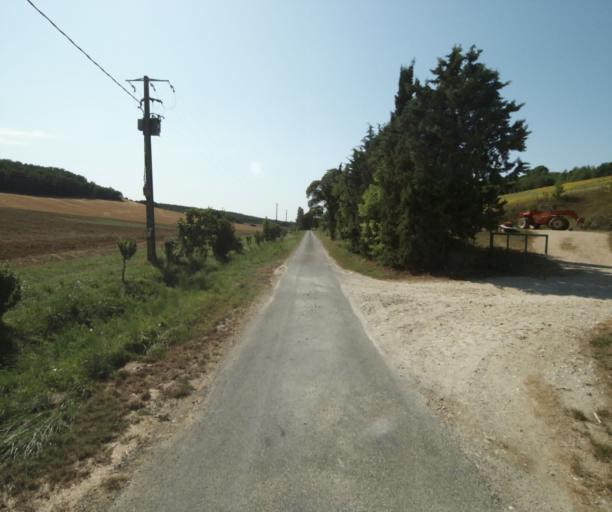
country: FR
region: Midi-Pyrenees
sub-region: Departement de la Haute-Garonne
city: Saint-Felix-Lauragais
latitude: 43.4366
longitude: 1.8439
